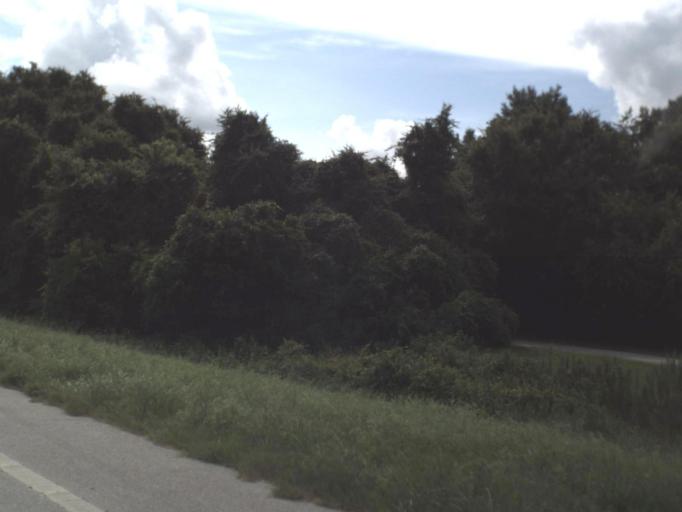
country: US
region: Florida
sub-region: Hillsborough County
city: Thonotosassa
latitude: 28.0796
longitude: -82.2832
